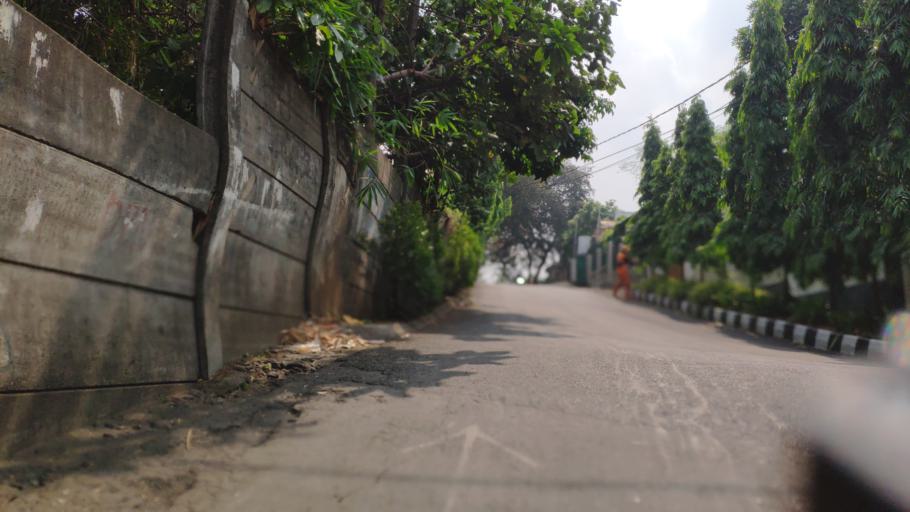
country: ID
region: West Java
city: Pamulang
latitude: -6.3071
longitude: 106.8087
